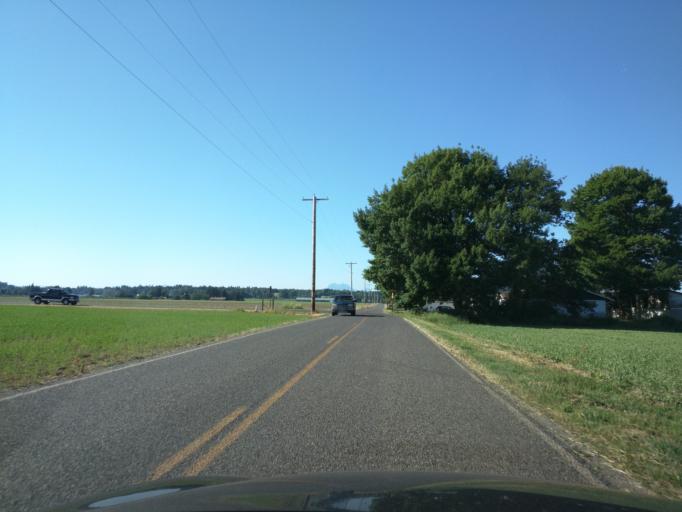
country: US
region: Washington
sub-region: Whatcom County
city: Lynden
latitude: 48.9858
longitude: -122.4519
